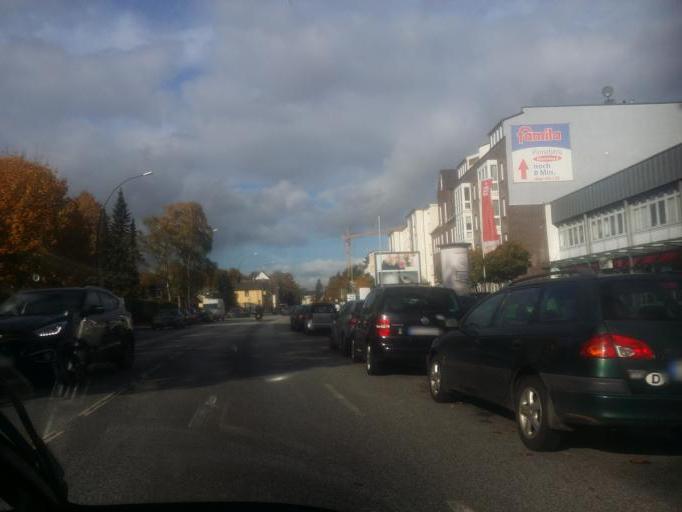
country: DE
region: Hamburg
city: Eidelstedt
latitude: 53.5922
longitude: 9.8718
